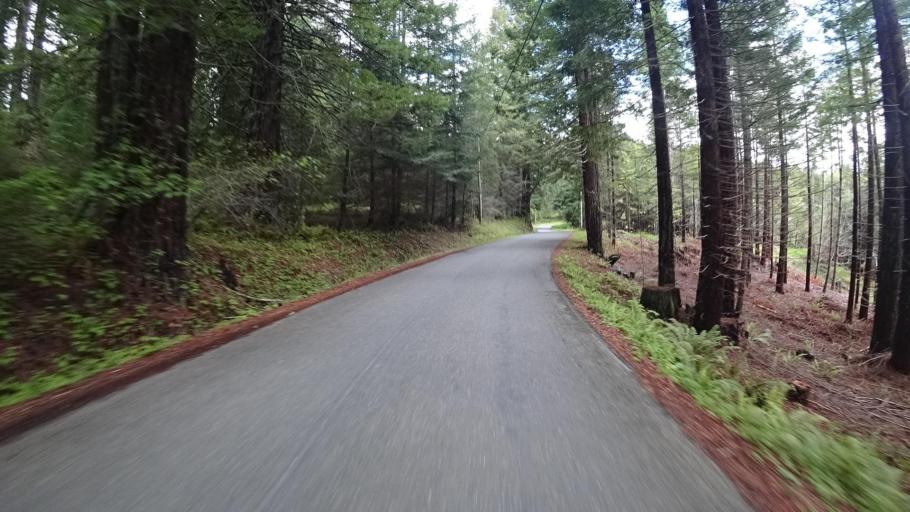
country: US
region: California
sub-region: Humboldt County
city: Blue Lake
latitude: 40.8564
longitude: -123.9318
